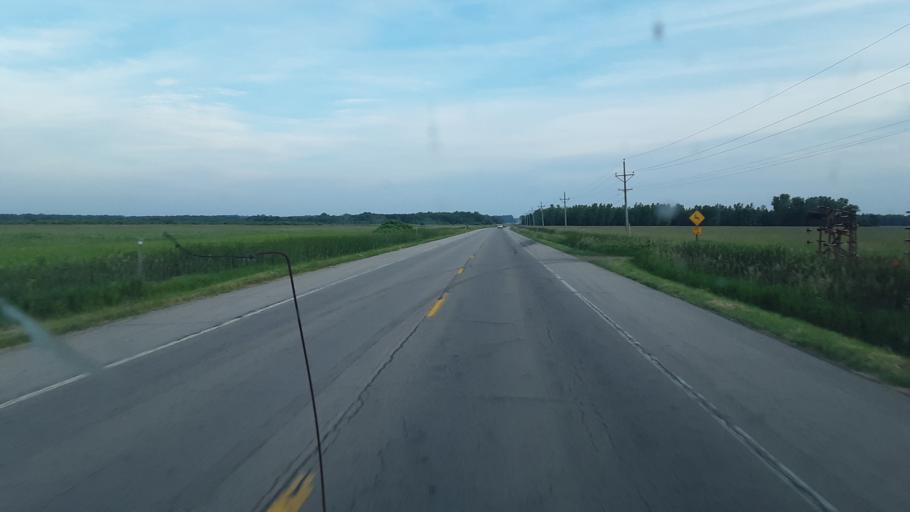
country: US
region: Iowa
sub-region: Benton County
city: Belle Plaine
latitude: 41.8791
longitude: -92.2780
